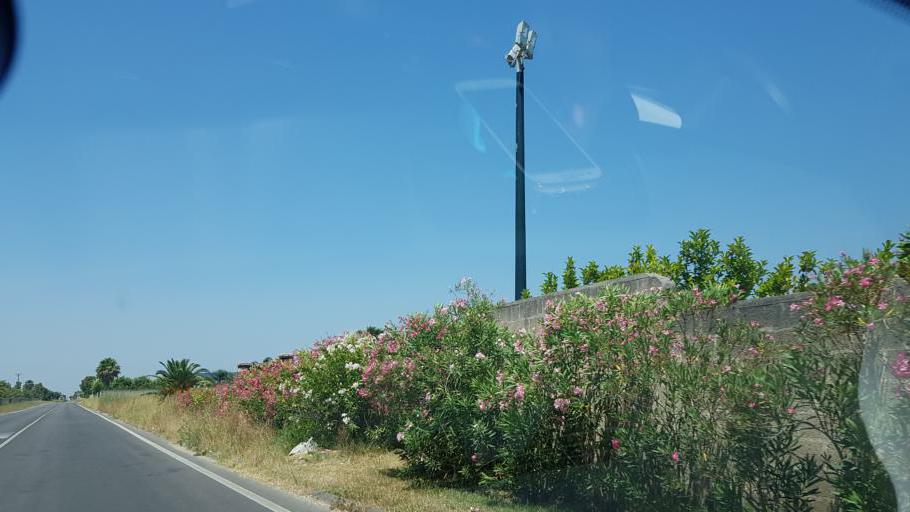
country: IT
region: Apulia
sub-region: Provincia di Lecce
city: Salice Salentino
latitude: 40.3641
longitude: 17.9676
